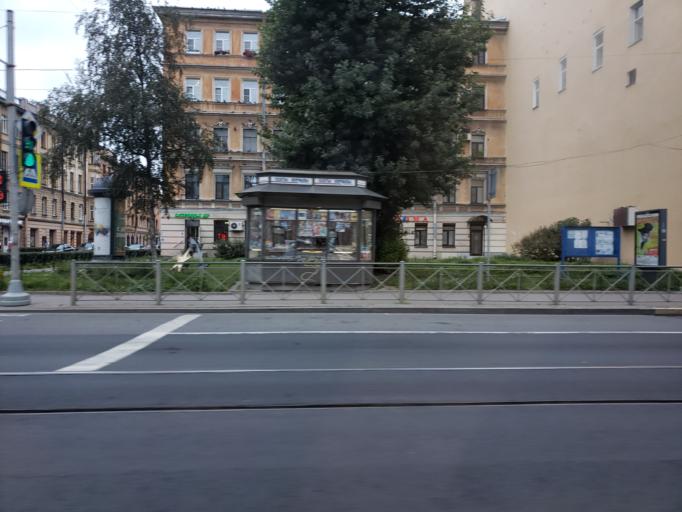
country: RU
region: St.-Petersburg
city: Petrogradka
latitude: 59.9556
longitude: 30.3287
